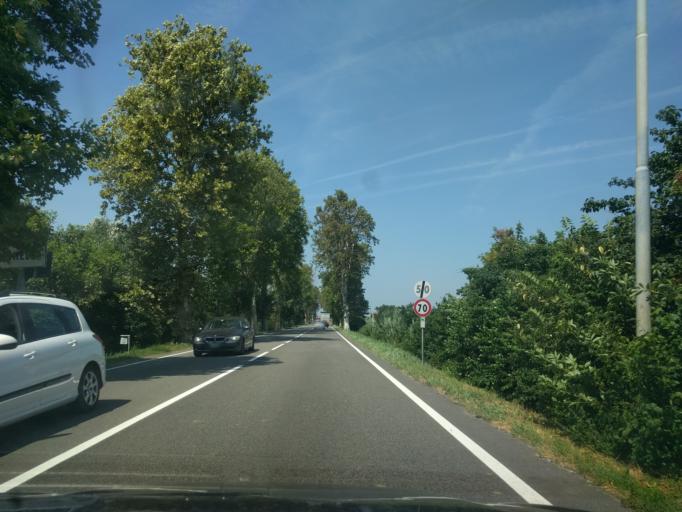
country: IT
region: Veneto
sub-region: Provincia di Padova
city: Stanghella
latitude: 45.1402
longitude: 11.7570
